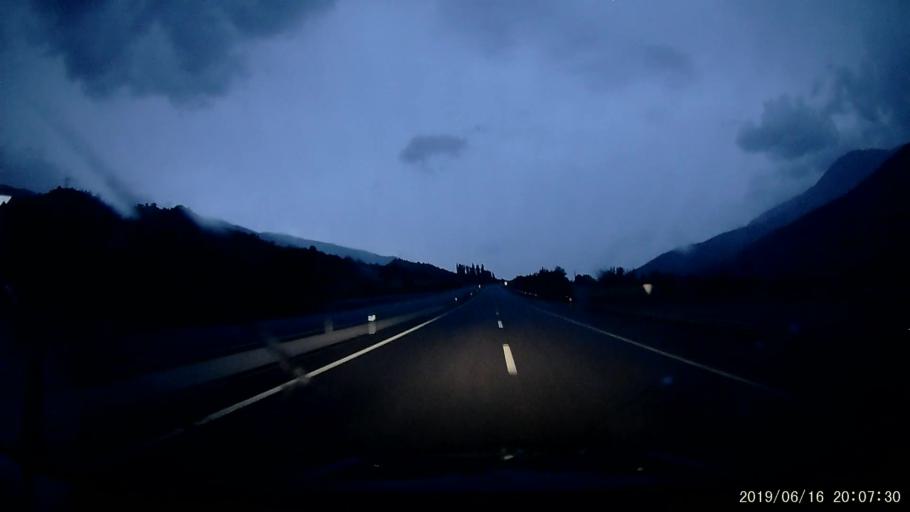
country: TR
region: Sivas
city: Dogansar
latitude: 40.3185
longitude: 37.6229
